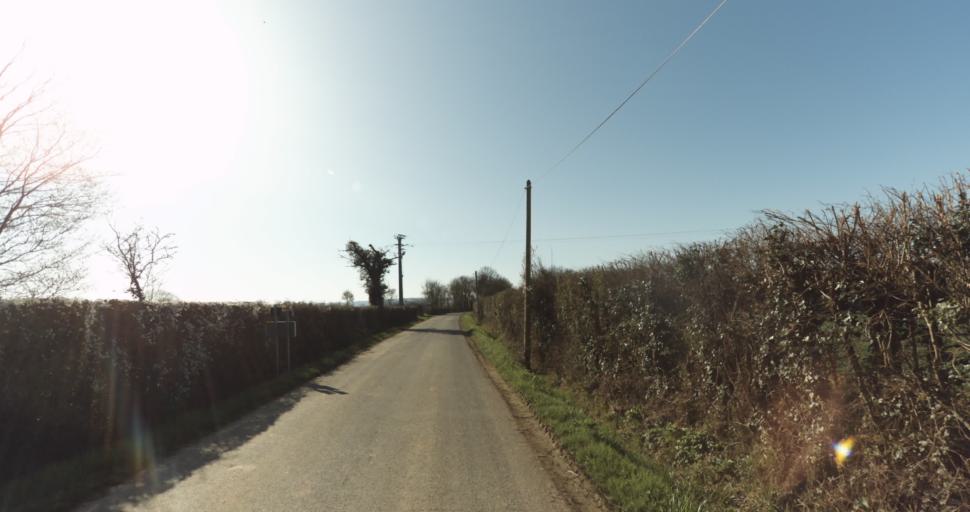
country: FR
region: Lower Normandy
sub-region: Departement du Calvados
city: Saint-Pierre-sur-Dives
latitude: 48.9978
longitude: -0.0043
